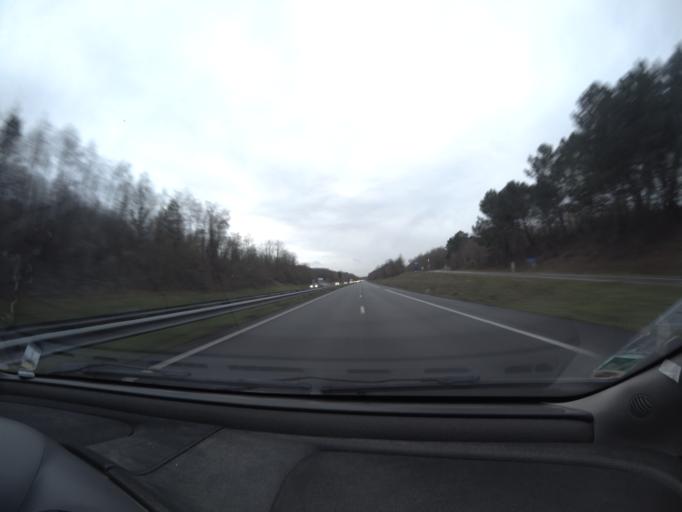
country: FR
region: Pays de la Loire
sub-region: Departement de Maine-et-Loire
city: Baune
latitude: 47.5213
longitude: -0.3616
